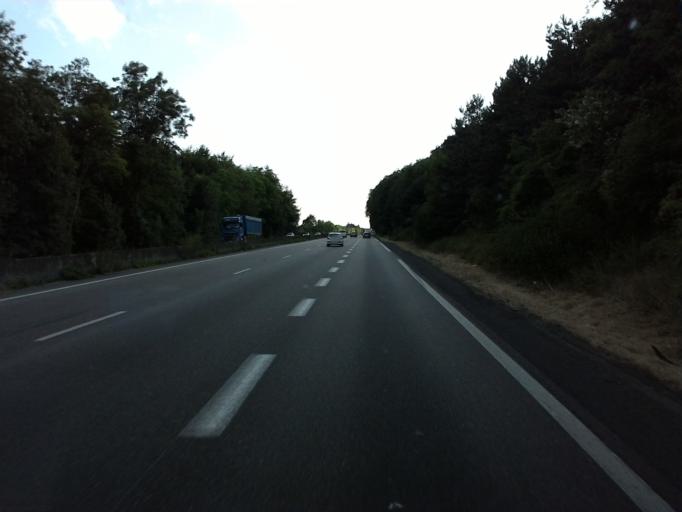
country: FR
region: Lorraine
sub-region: Departement de Meurthe-et-Moselle
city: Maxeville
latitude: 48.7100
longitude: 6.1447
